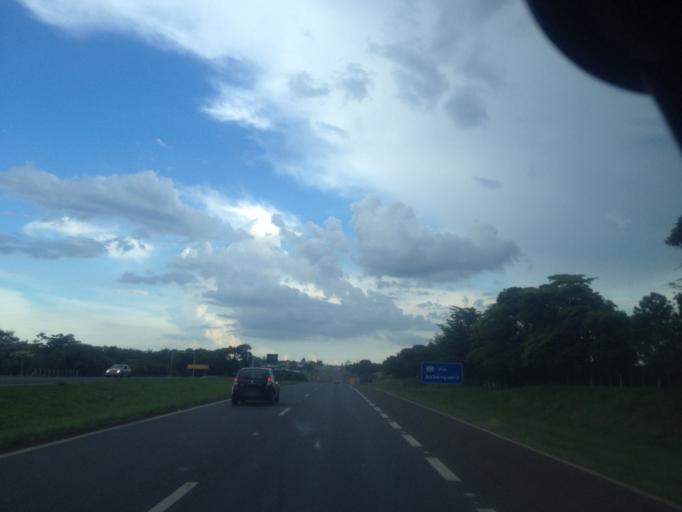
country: BR
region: Sao Paulo
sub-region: Pirassununga
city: Pirassununga
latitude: -22.0190
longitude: -47.4388
